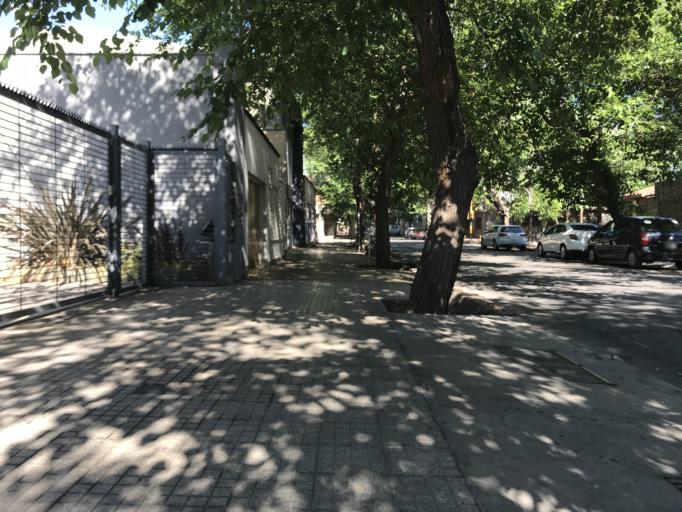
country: AR
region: Mendoza
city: Mendoza
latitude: -32.8766
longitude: -68.8330
